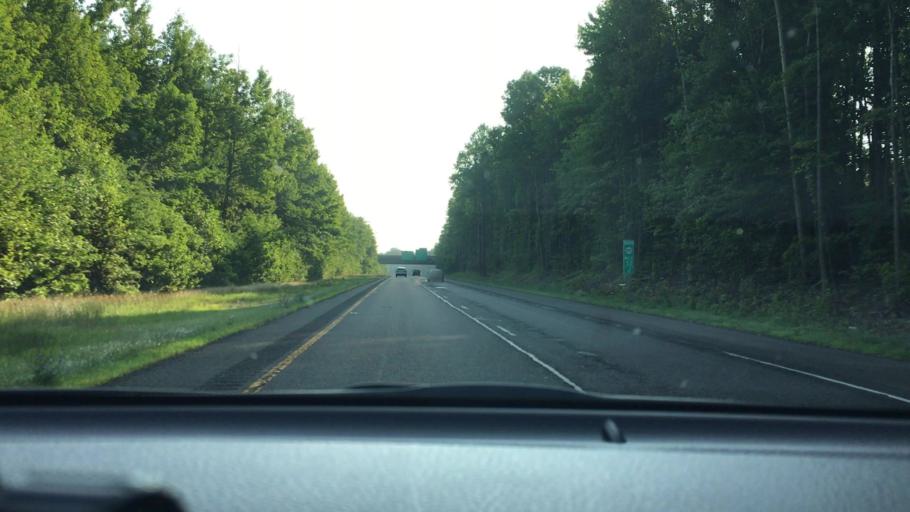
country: US
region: New Jersey
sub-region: Gloucester County
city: Pitman
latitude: 39.7543
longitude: -75.1335
